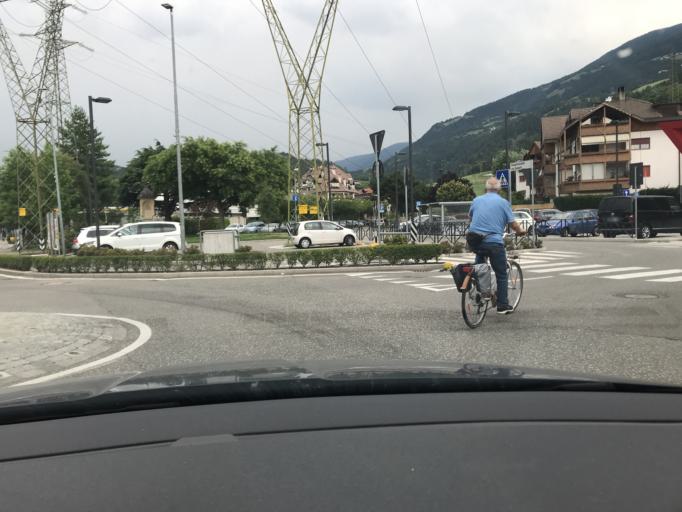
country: IT
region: Trentino-Alto Adige
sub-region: Bolzano
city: Bressanone
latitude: 46.7089
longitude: 11.6615
